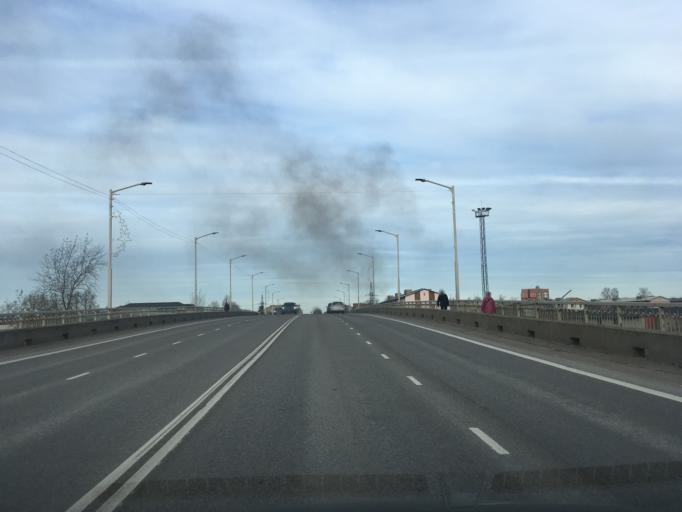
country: EE
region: Ida-Virumaa
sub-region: Narva linn
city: Narva
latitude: 59.3711
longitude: 28.1843
